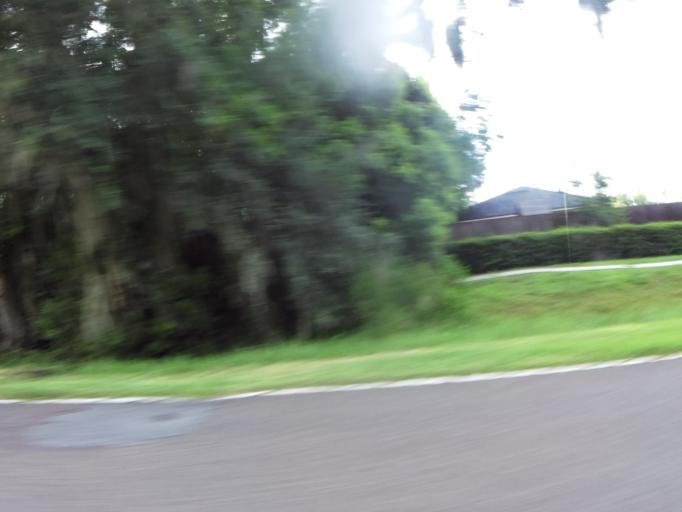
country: US
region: Florida
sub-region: Nassau County
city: Nassau Village-Ratliff
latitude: 30.4158
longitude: -81.7648
